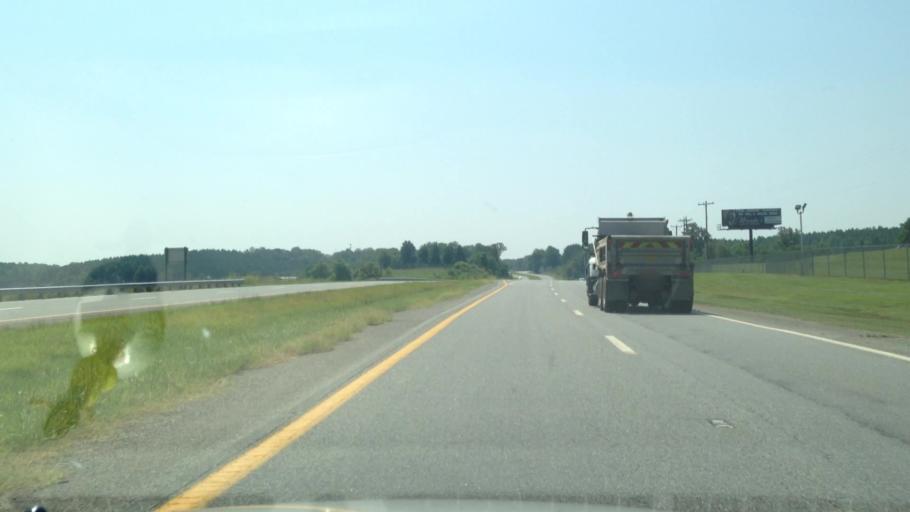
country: US
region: Virginia
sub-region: Patrick County
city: Patrick Springs
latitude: 36.5985
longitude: -80.1570
